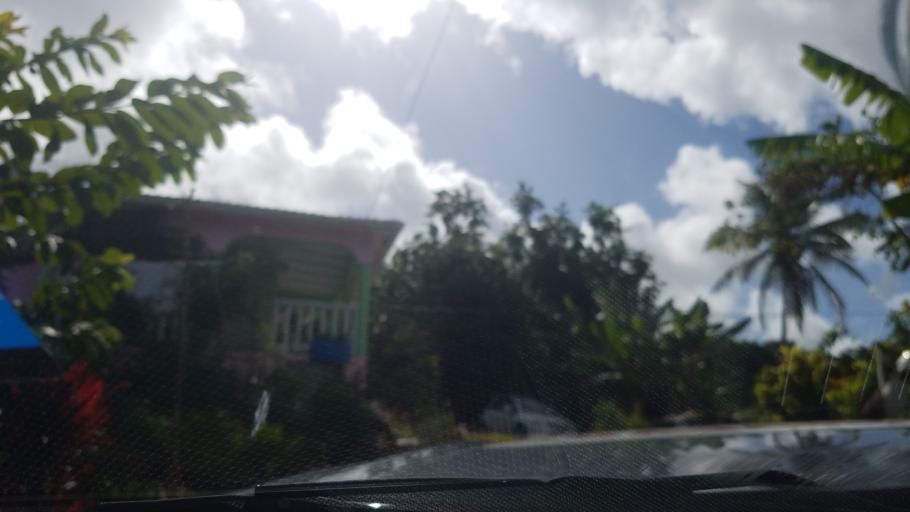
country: LC
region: Castries Quarter
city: Bisee
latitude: 14.0064
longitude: -60.9549
